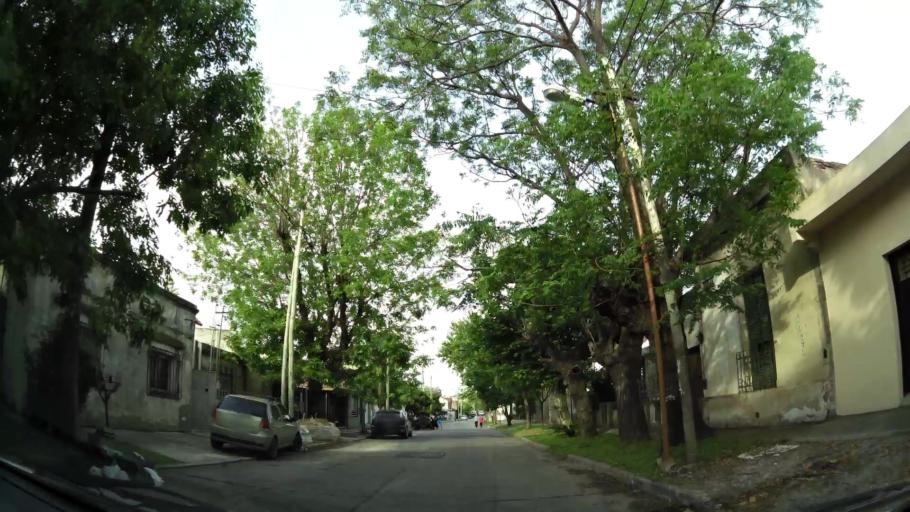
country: AR
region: Buenos Aires
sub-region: Partido de Quilmes
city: Quilmes
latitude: -34.7369
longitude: -58.2672
